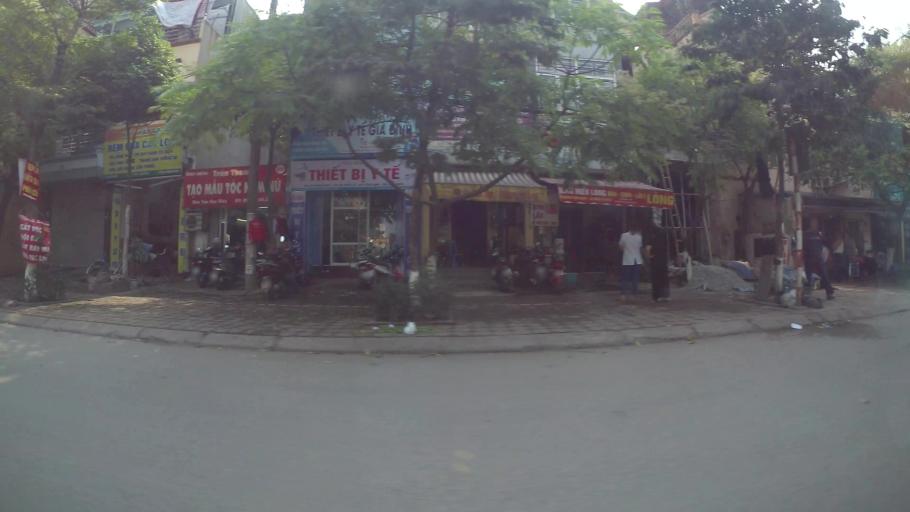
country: VN
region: Ha Noi
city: Thanh Xuan
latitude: 20.9736
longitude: 105.8248
